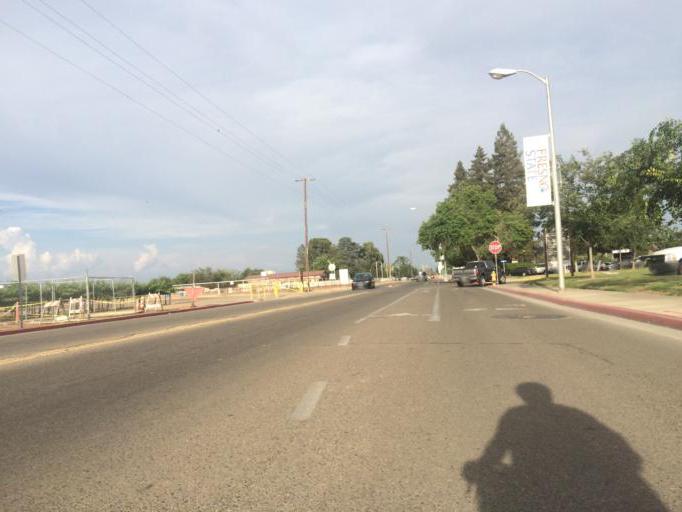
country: US
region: California
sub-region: Fresno County
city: Clovis
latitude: 36.8158
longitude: -119.7459
